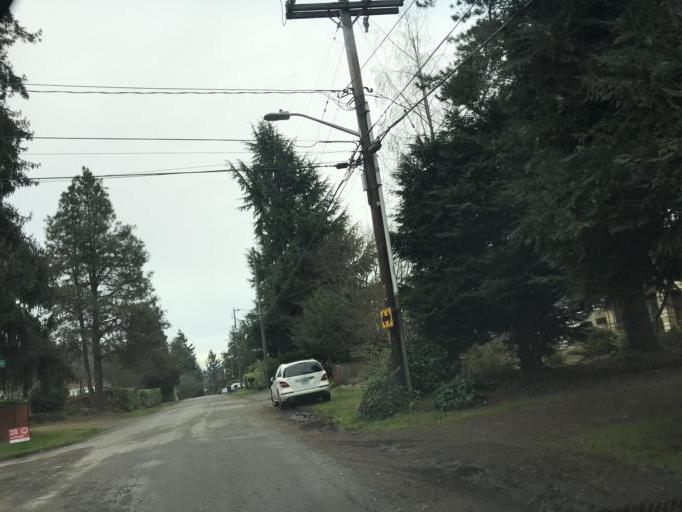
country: US
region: Washington
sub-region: King County
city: Lake Forest Park
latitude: 47.7046
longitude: -122.3068
